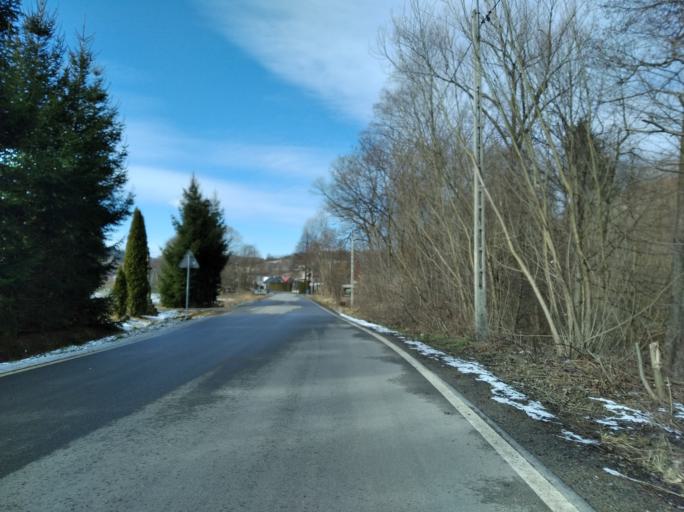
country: PL
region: Subcarpathian Voivodeship
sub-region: Powiat brzozowski
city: Jasienica Rosielna
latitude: 49.7547
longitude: 21.8952
